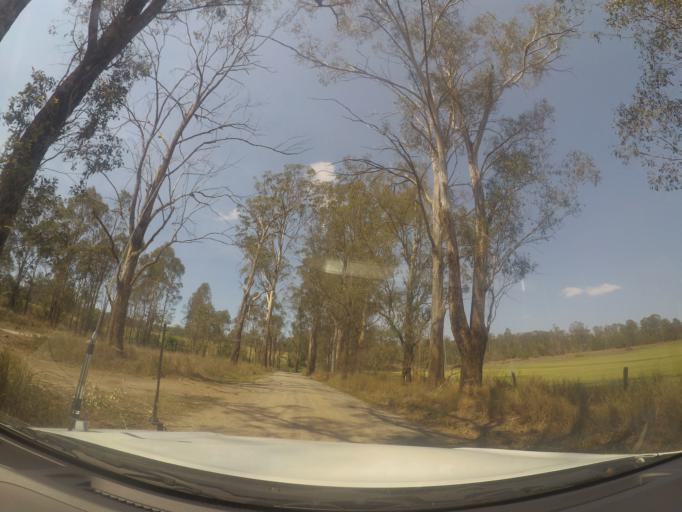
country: AU
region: Queensland
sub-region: Logan
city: North Maclean
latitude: -27.7716
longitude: 153.0387
